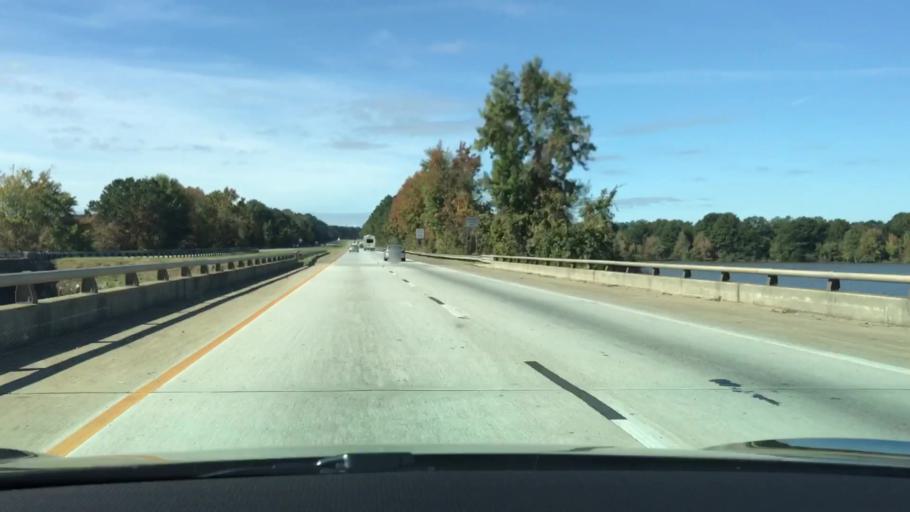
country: US
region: Georgia
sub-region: Putnam County
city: Jefferson
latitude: 33.5342
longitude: -83.2722
